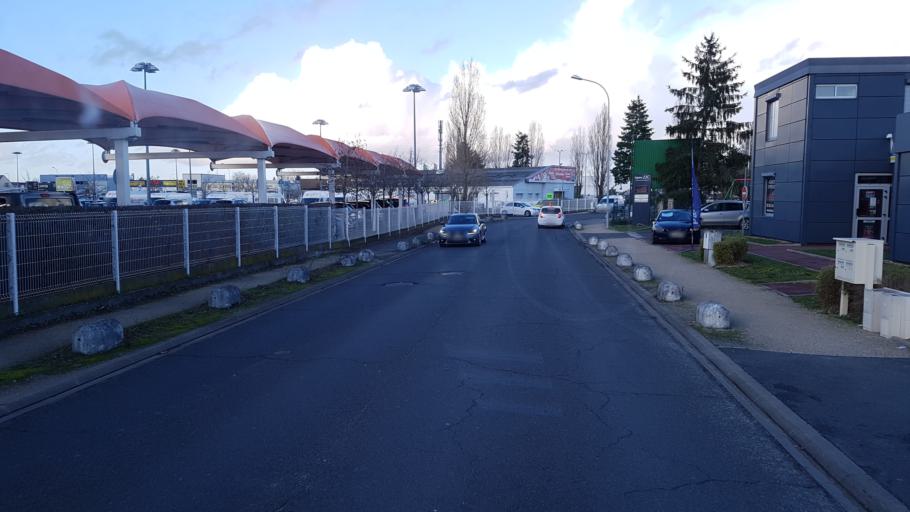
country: FR
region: Centre
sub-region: Departement du Loiret
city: Olivet
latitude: 47.8416
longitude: 1.9186
